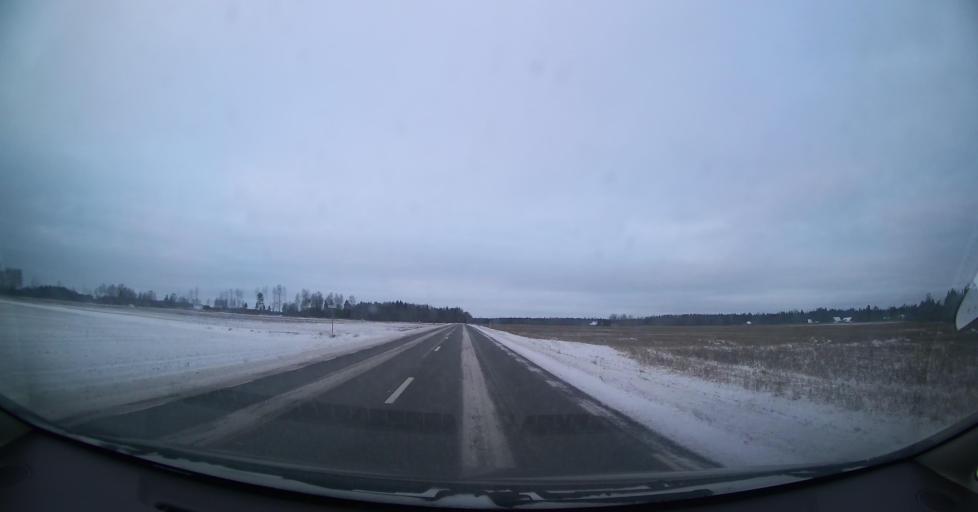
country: EE
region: Harju
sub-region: Anija vald
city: Kehra
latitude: 59.2800
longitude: 25.3678
